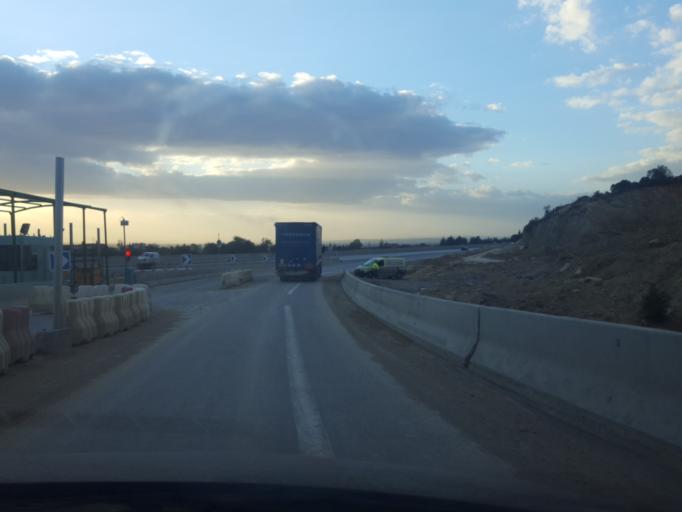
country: TN
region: Tunis
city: La Sebala du Mornag
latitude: 36.6467
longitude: 10.3634
